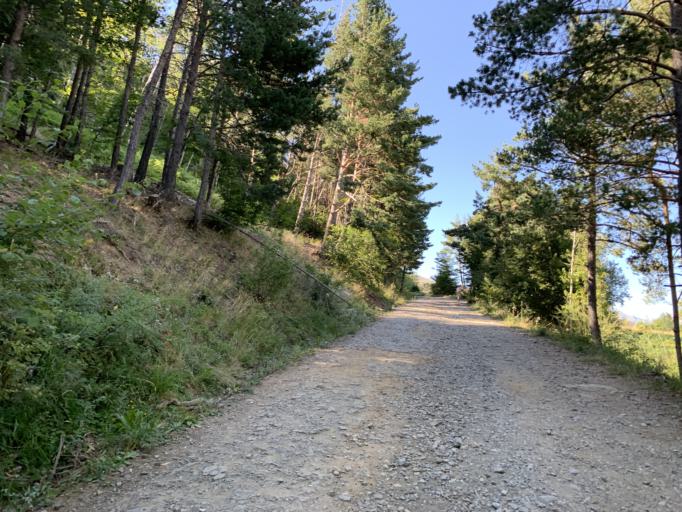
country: ES
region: Aragon
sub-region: Provincia de Huesca
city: Hoz de Jaca
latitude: 42.6978
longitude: -0.3340
